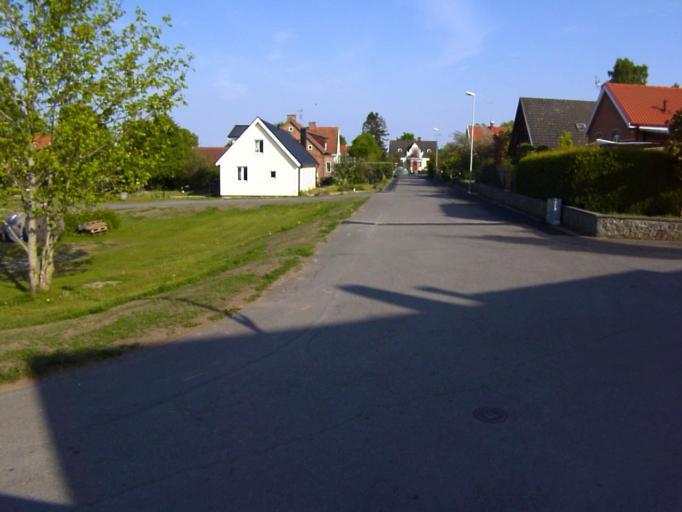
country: SE
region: Skane
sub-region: Kristianstads Kommun
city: Onnestad
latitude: 56.0607
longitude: 14.0258
